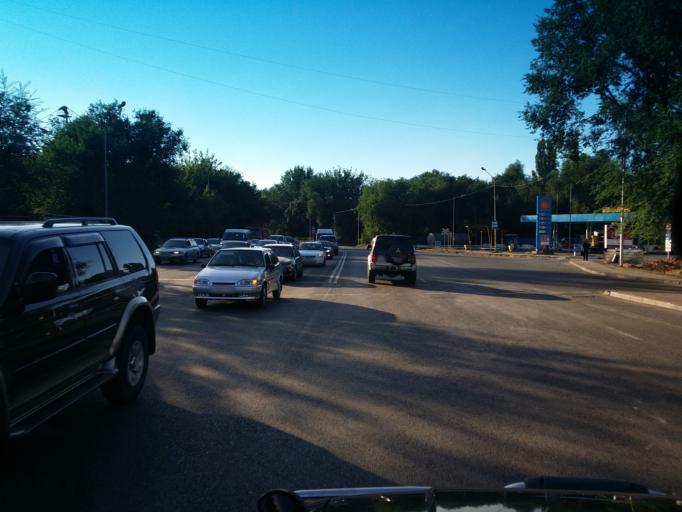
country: KZ
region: Almaty Oblysy
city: Pervomayskiy
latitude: 43.3468
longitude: 76.9689
